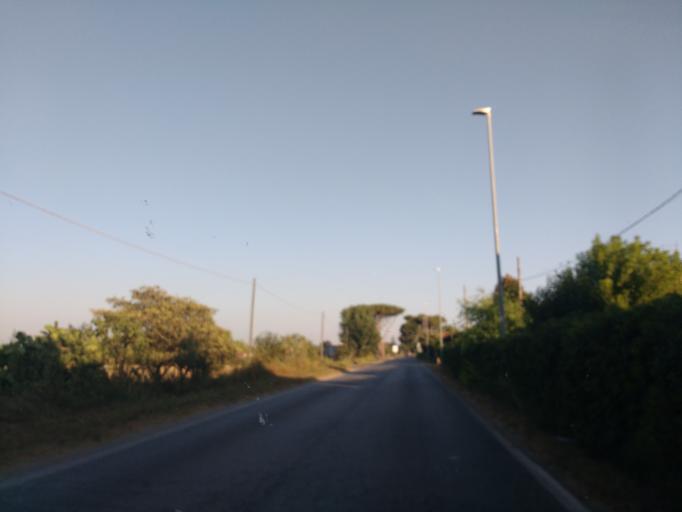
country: IT
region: Latium
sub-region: Citta metropolitana di Roma Capitale
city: Maccarese
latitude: 41.8600
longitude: 12.2131
